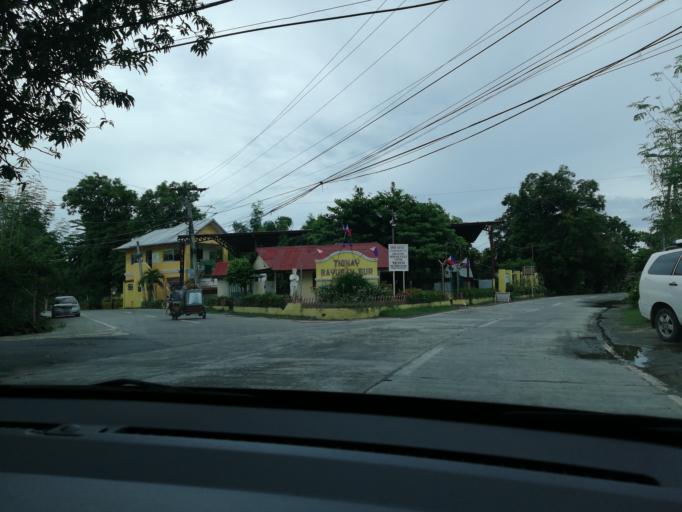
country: PH
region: Ilocos
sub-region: Province of Ilocos Sur
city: Bantay
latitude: 17.5850
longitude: 120.3808
